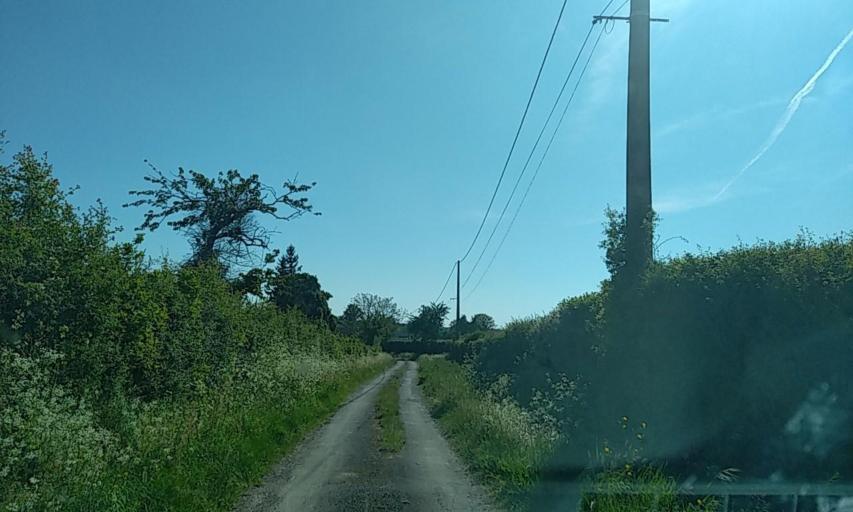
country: FR
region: Poitou-Charentes
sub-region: Departement des Deux-Sevres
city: Boisme
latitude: 46.7791
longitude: -0.4060
